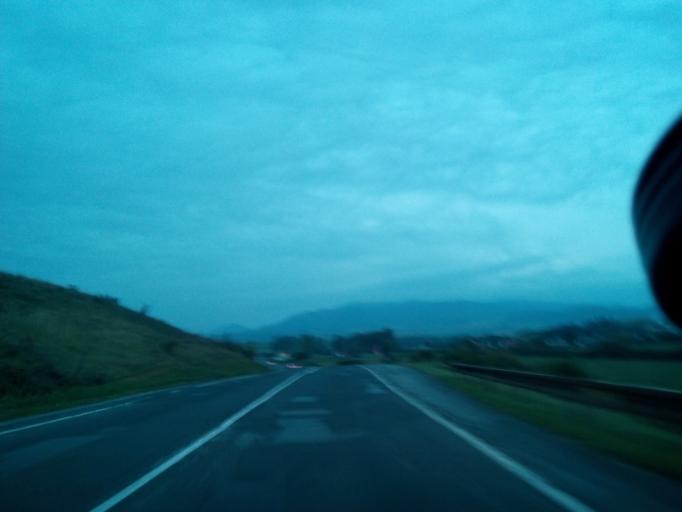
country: SK
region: Presovsky
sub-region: Okres Presov
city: Presov
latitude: 49.0730
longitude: 21.3300
